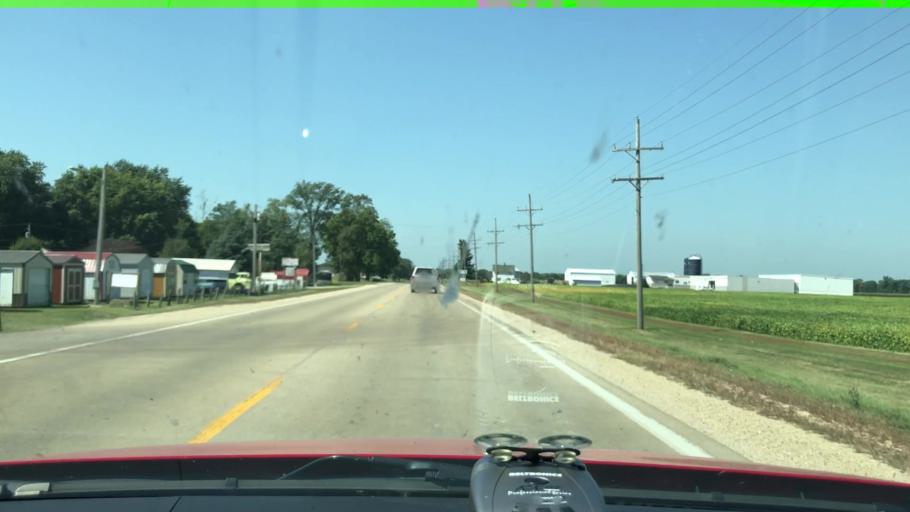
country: US
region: Illinois
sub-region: Whiteside County
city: Sterling
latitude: 41.7724
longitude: -89.7258
